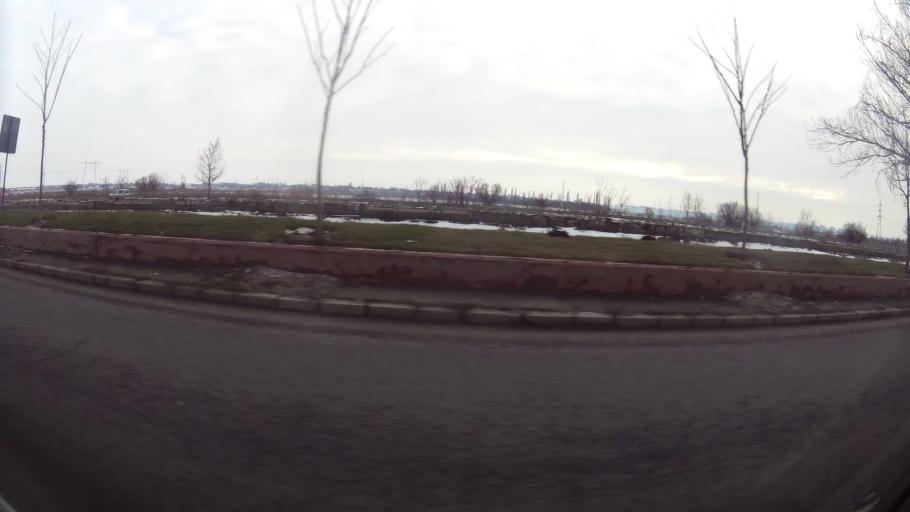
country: RO
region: Ilfov
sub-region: Comuna Popesti-Leordeni
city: Popesti-Leordeni
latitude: 44.3943
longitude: 26.1809
